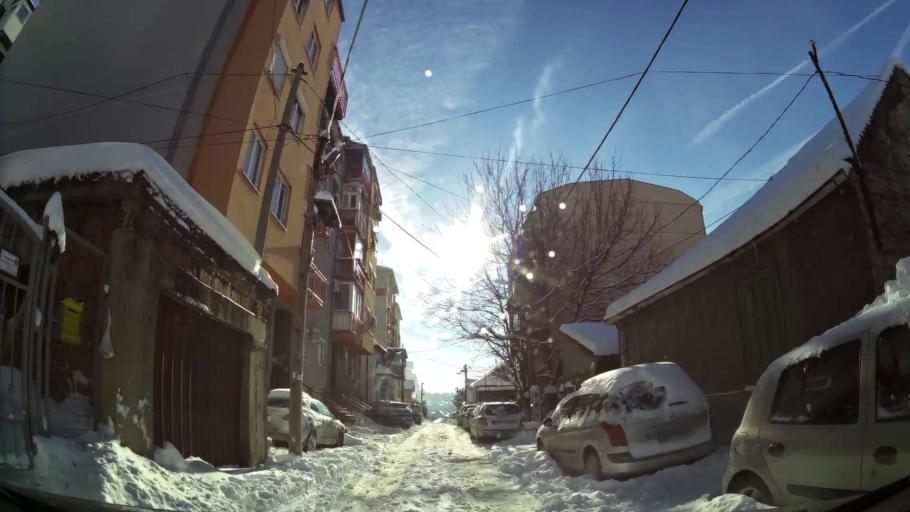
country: RS
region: Central Serbia
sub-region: Belgrade
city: Palilula
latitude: 44.7918
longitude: 20.5027
